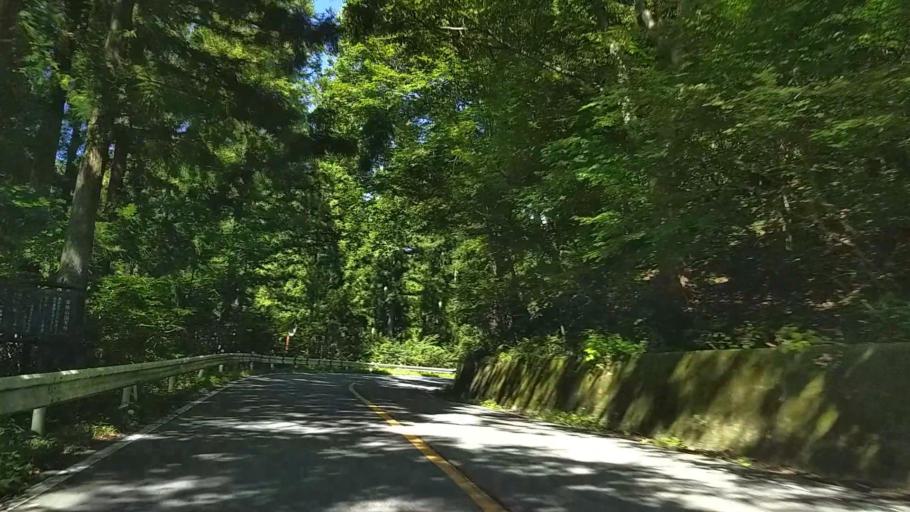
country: JP
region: Gunma
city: Annaka
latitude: 36.3565
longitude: 138.7024
